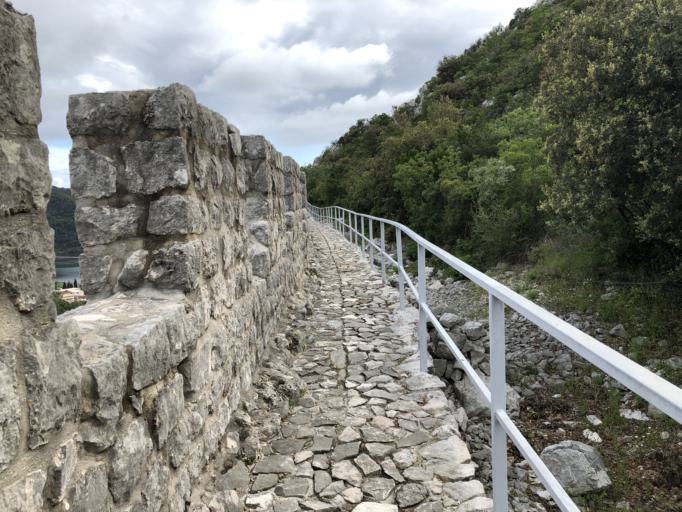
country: HR
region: Dubrovacko-Neretvanska
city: Ston
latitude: 42.8428
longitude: 17.6990
